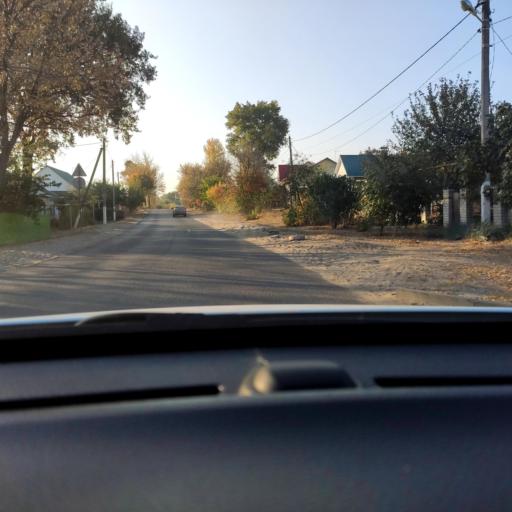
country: RU
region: Voronezj
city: Somovo
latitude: 51.6920
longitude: 39.3178
